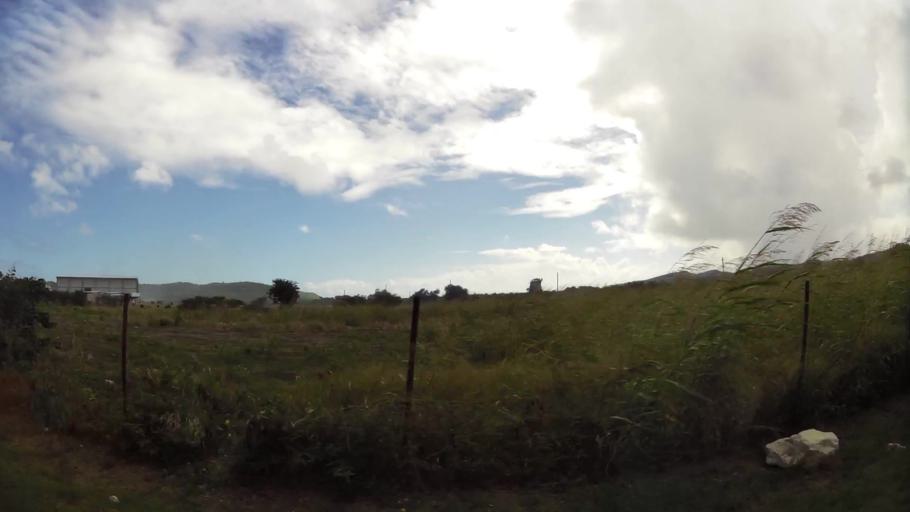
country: AG
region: Saint Paul
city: Liberta
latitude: 17.0522
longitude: -61.7477
